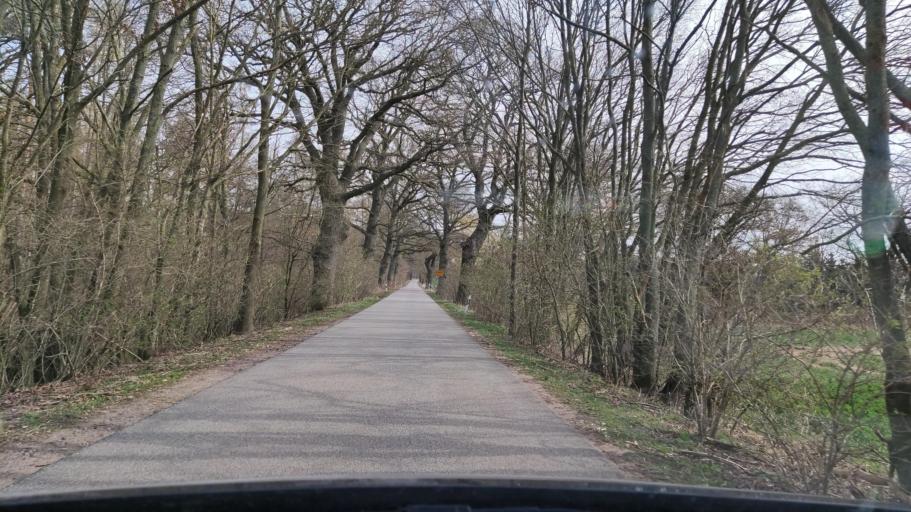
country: DE
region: Mecklenburg-Vorpommern
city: Robel
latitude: 53.3483
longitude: 12.5514
